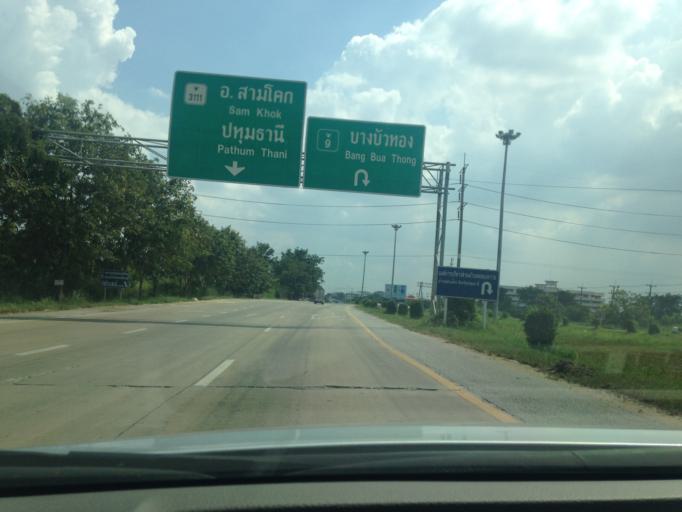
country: TH
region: Pathum Thani
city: Sam Khok
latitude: 14.0891
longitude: 100.5197
